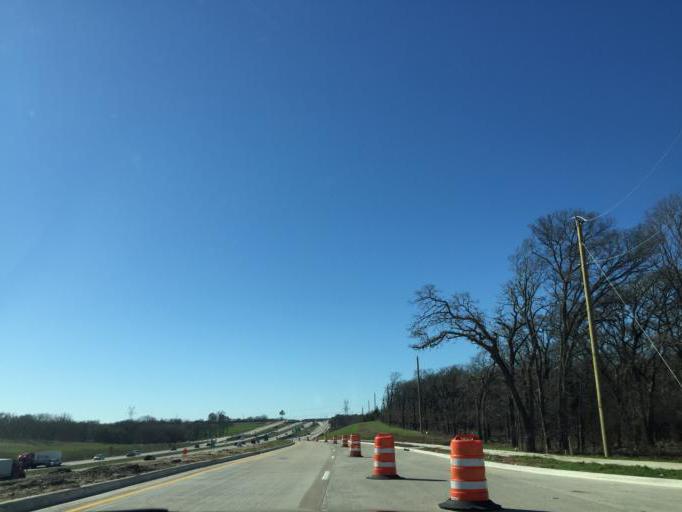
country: US
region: Texas
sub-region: Parker County
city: Hudson Oaks
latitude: 32.7483
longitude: -97.7293
